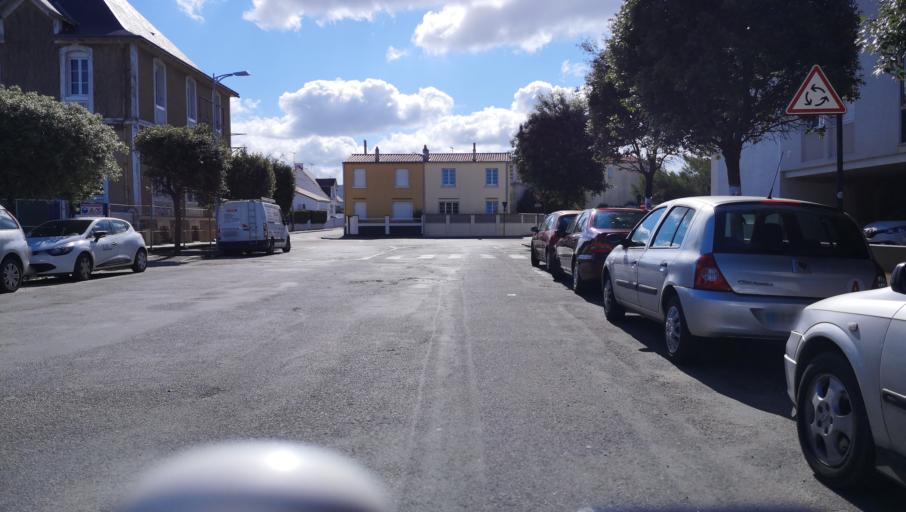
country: FR
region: Pays de la Loire
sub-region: Departement de la Vendee
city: Les Sables-d'Olonne
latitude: 46.4887
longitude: -1.7620
